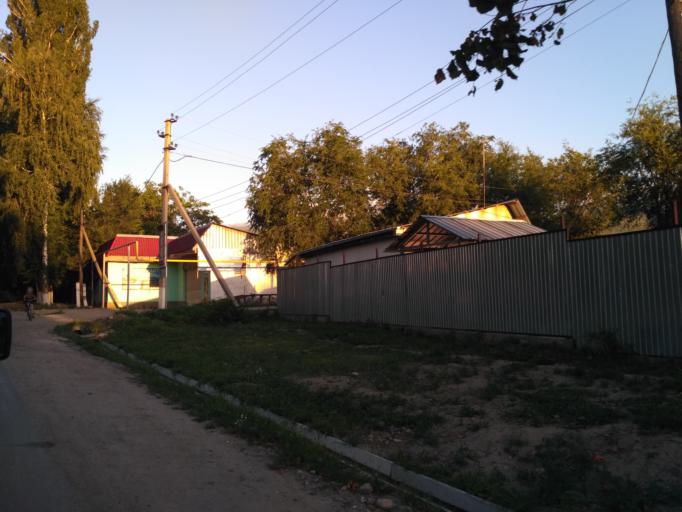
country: KZ
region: Almaty Qalasy
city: Almaty
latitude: 43.1769
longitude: 76.7585
